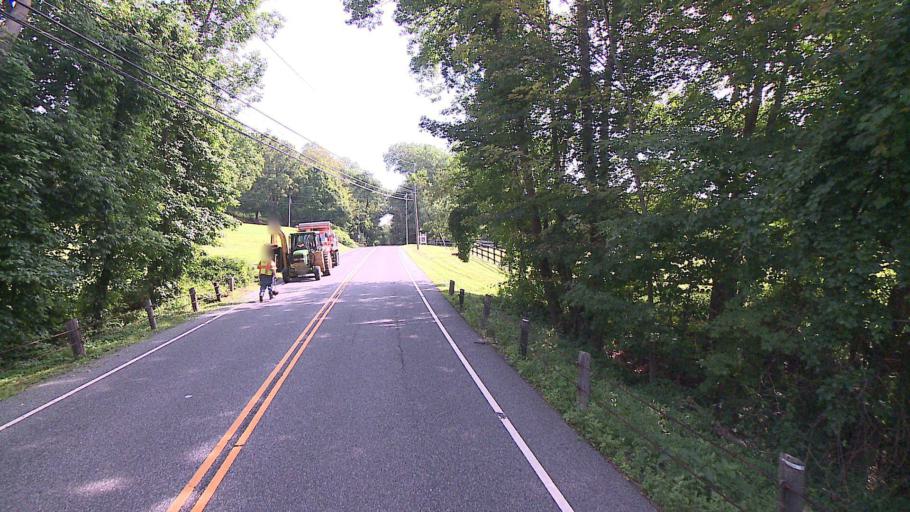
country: US
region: Connecticut
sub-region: Fairfield County
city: Sherman
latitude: 41.5373
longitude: -73.5027
